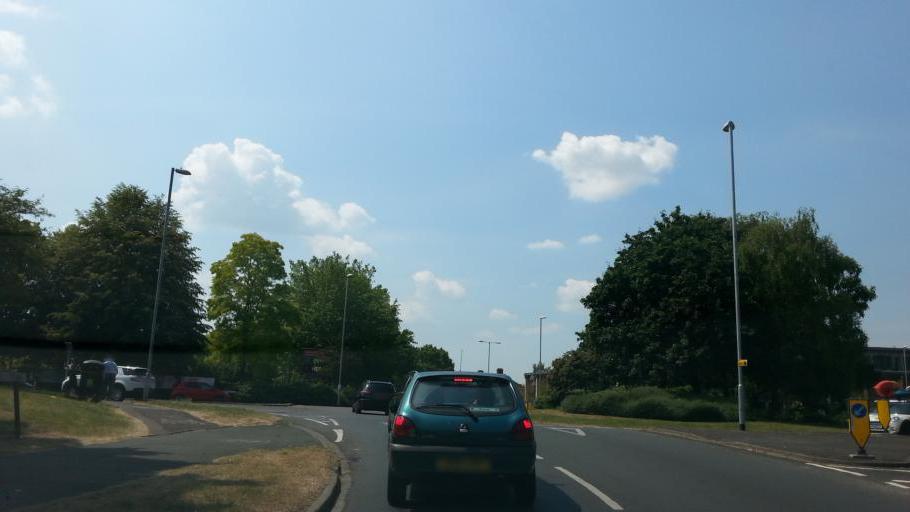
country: GB
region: England
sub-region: Cambridgeshire
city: Cambridge
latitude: 52.2009
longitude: 0.1589
